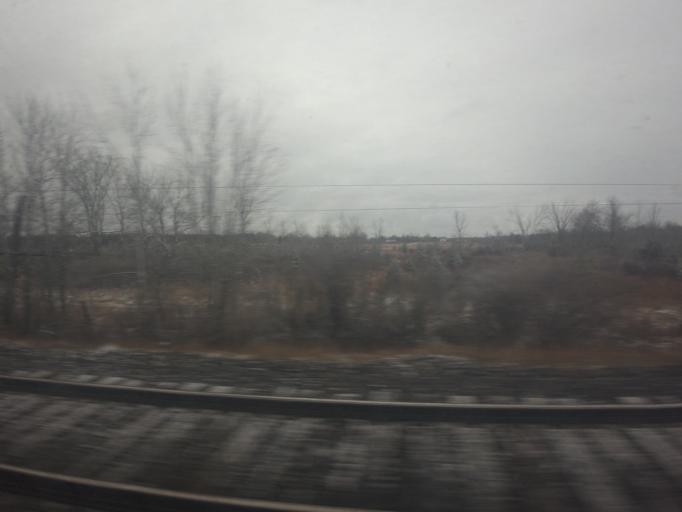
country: CA
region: Ontario
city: Gananoque
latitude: 44.3766
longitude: -76.0851
